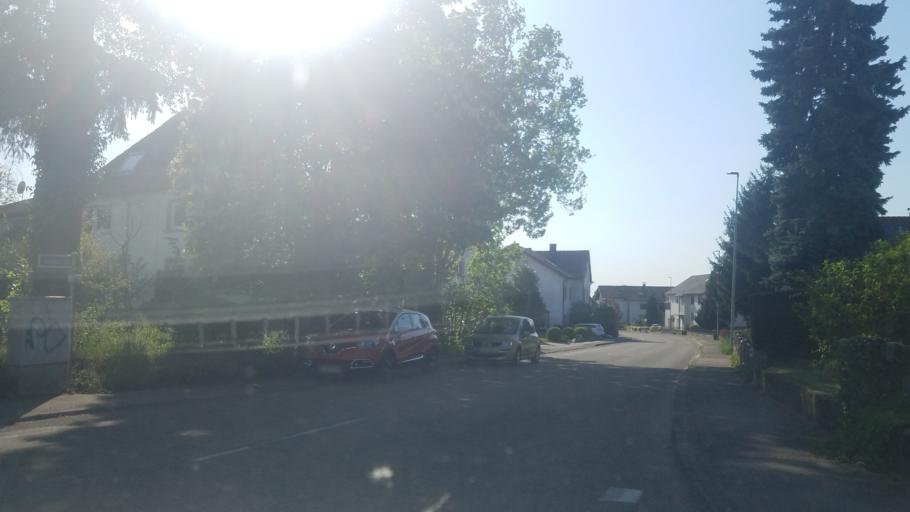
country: DE
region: Baden-Wuerttemberg
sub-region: Karlsruhe Region
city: Buhl
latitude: 48.6873
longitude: 8.1468
